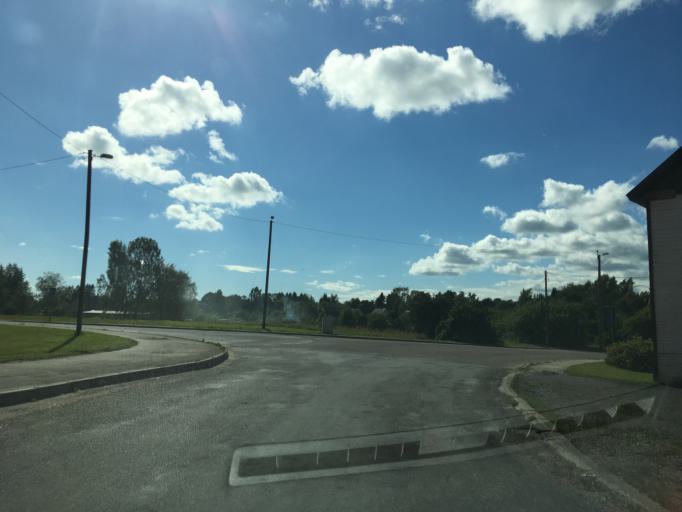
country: EE
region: Paernumaa
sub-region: Vaendra vald (alev)
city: Vandra
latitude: 58.6484
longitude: 25.0315
